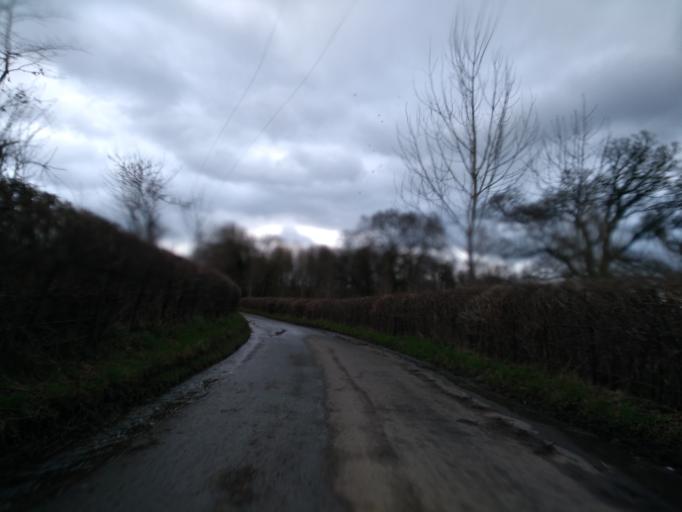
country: GB
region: England
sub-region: Devon
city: Crediton
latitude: 50.7921
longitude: -3.6269
